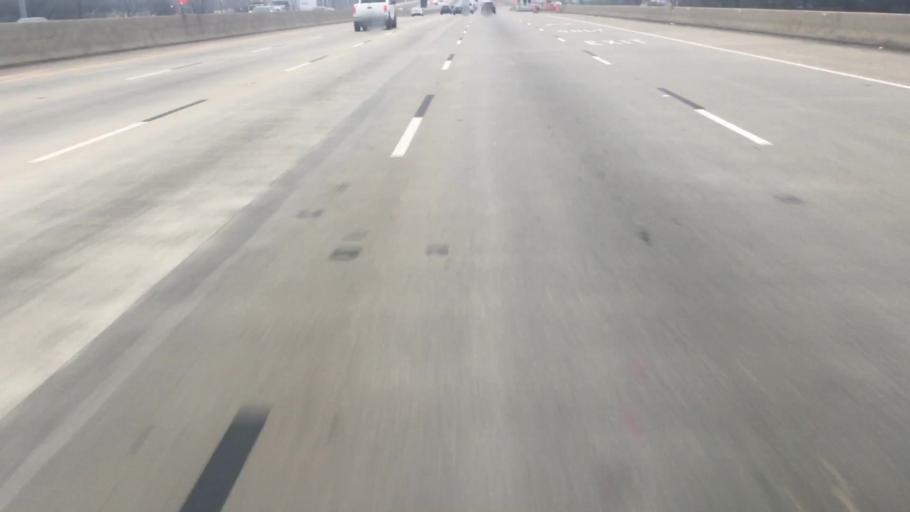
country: US
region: Alabama
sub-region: Jefferson County
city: Birmingham
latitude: 33.5466
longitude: -86.8281
